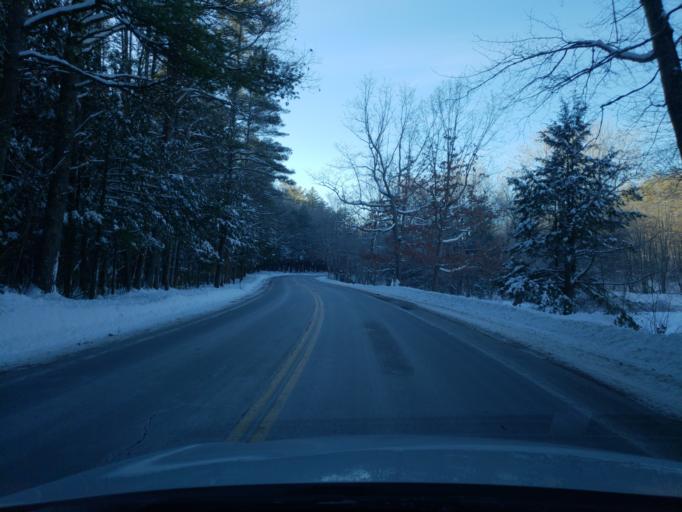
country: US
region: New Hampshire
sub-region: Hillsborough County
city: Goffstown
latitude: 43.0099
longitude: -71.6462
